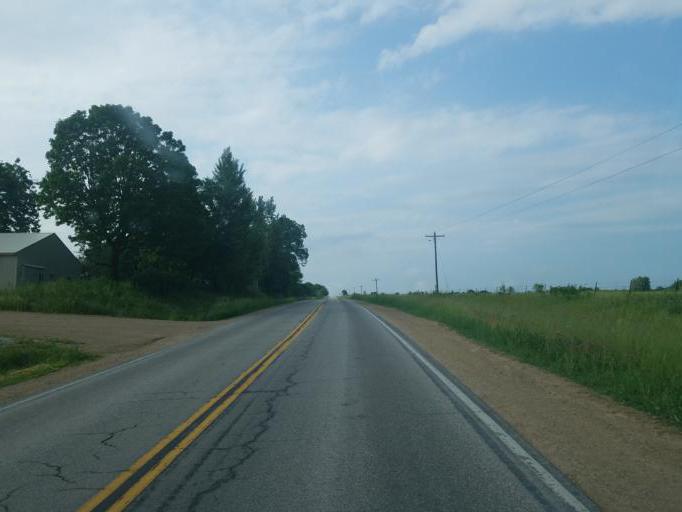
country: US
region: Wisconsin
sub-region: Vernon County
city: Hillsboro
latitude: 43.6311
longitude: -90.4526
